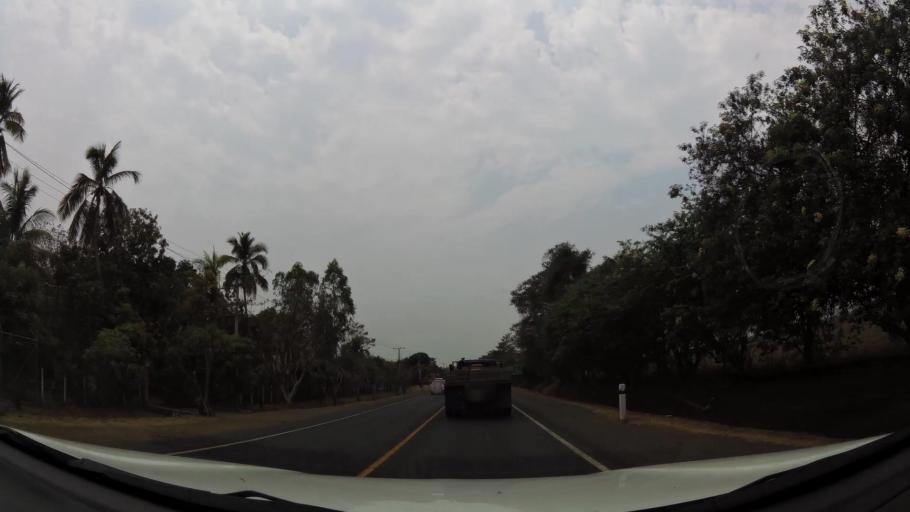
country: NI
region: Chinandega
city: Chichigalpa
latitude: 12.5907
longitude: -87.0219
